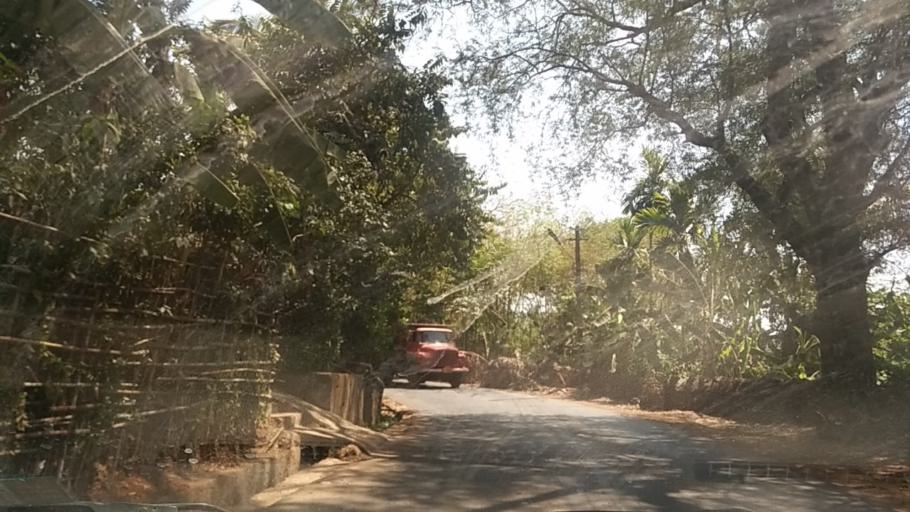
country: IN
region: Goa
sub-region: North Goa
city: Dicholi
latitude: 15.5798
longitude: 73.9237
